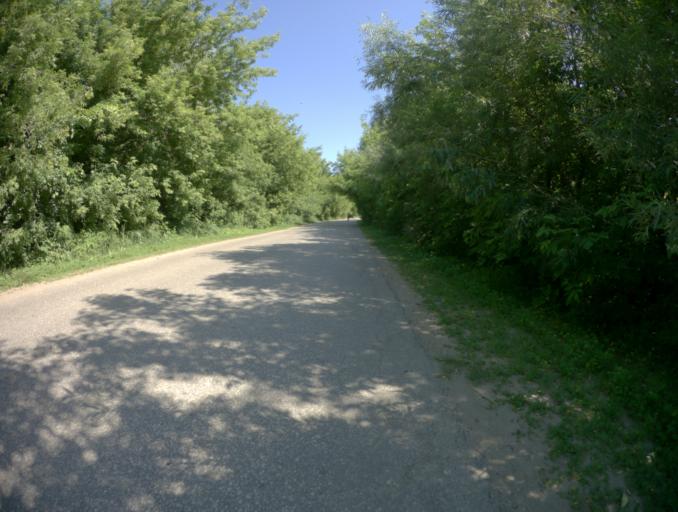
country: RU
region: Vladimir
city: Vyazniki
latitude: 56.2497
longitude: 42.1694
